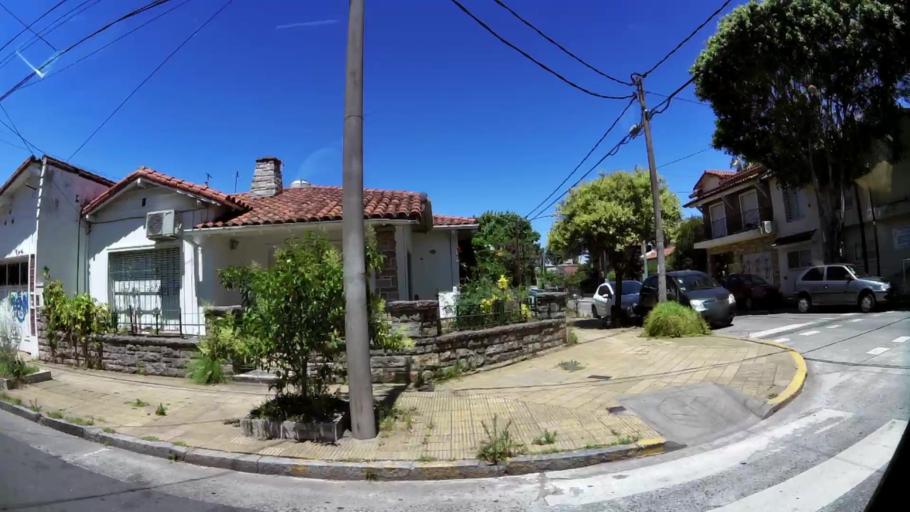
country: AR
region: Buenos Aires
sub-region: Partido de San Isidro
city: San Isidro
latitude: -34.4934
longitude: -58.5085
